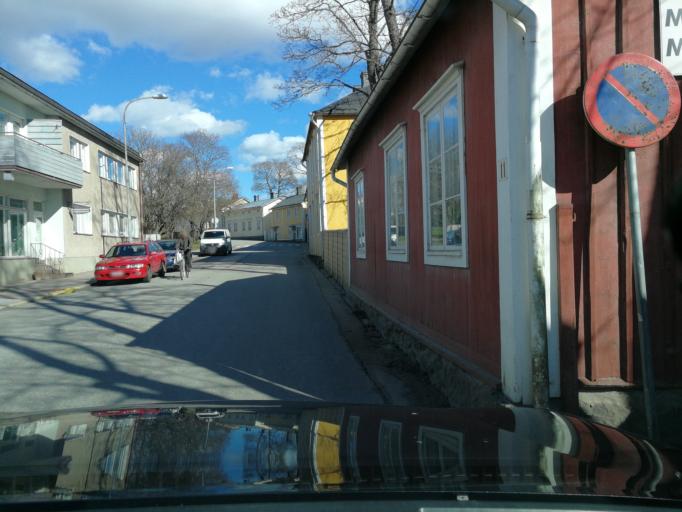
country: FI
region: Uusimaa
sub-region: Raaseporin
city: Ekenaes
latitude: 59.9742
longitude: 23.4377
